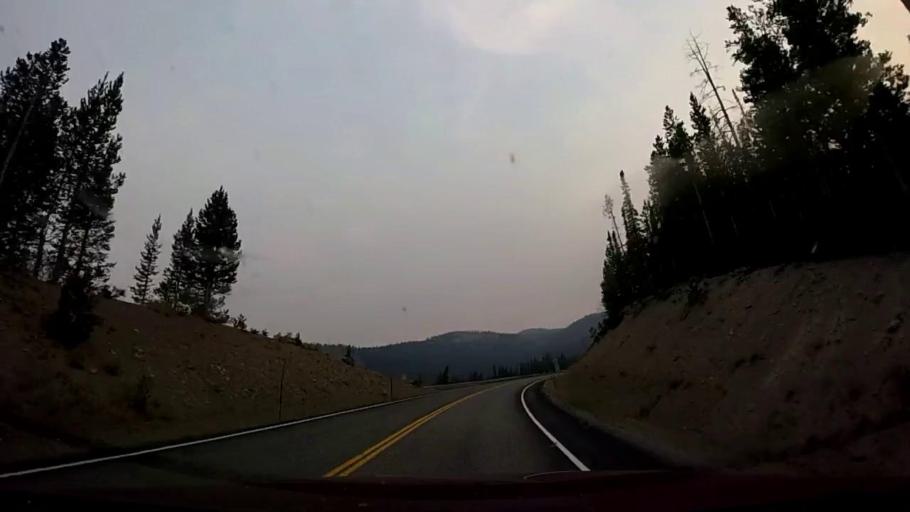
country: US
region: Idaho
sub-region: Blaine County
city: Ketchum
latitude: 43.8748
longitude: -114.7053
